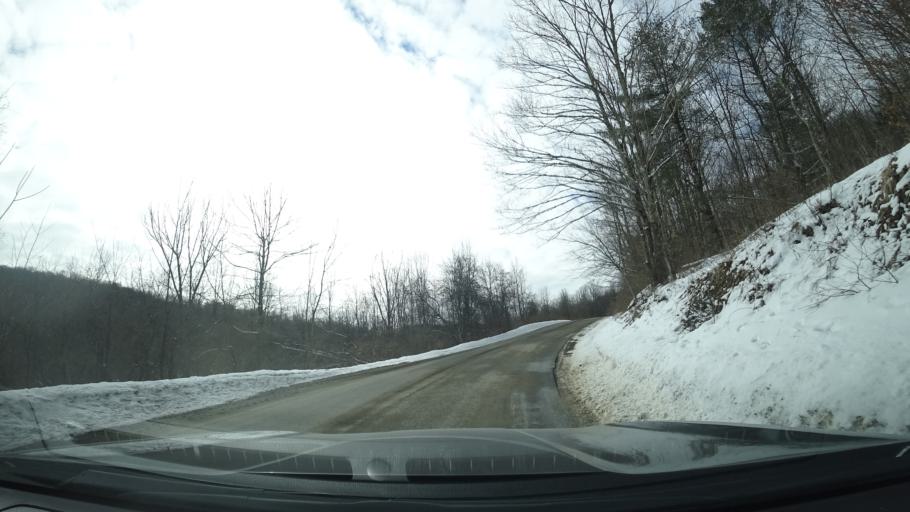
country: US
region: New York
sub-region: Washington County
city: Greenwich
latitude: 43.2190
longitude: -73.3554
